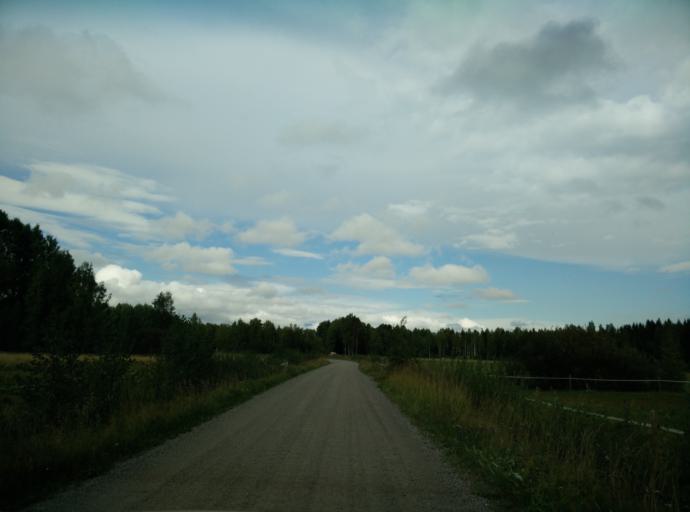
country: FI
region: Haeme
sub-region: Haemeenlinna
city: Kalvola
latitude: 61.1198
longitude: 24.1412
